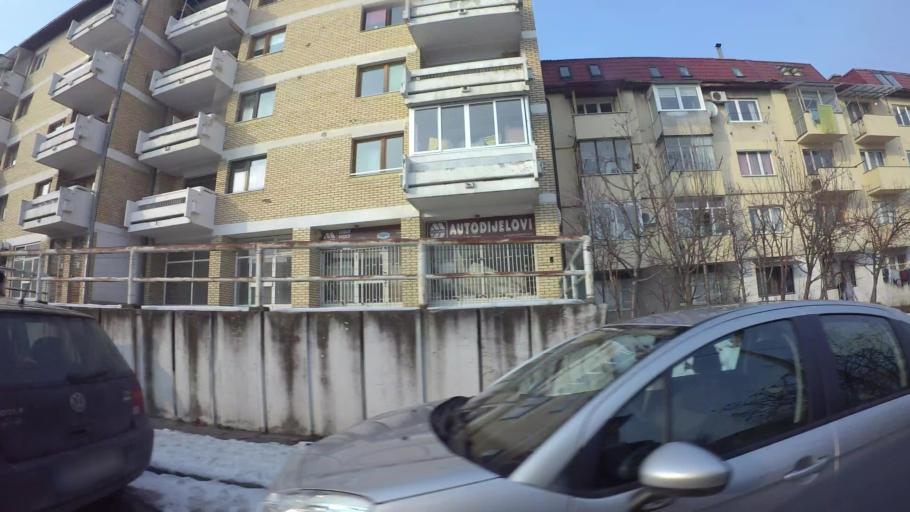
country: BA
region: Federation of Bosnia and Herzegovina
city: Kobilja Glava
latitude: 43.8661
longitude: 18.3983
